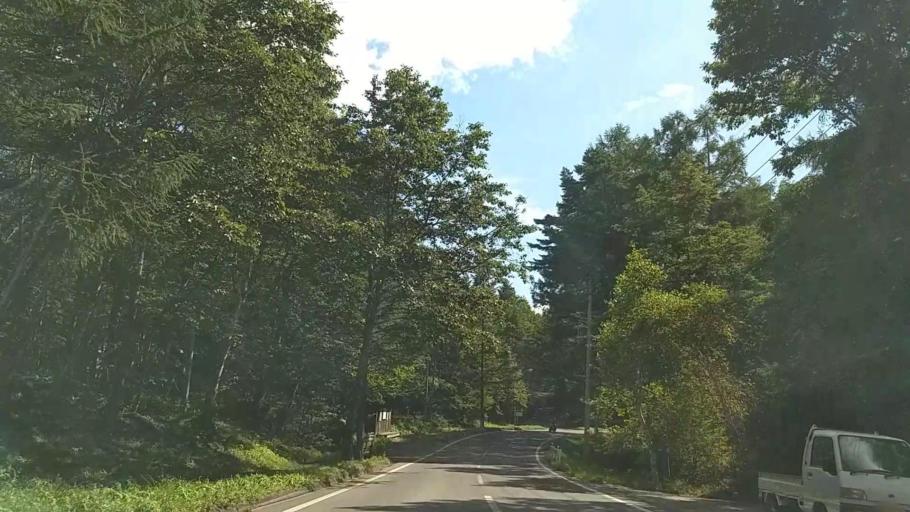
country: JP
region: Nagano
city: Chino
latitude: 36.1246
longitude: 138.2679
